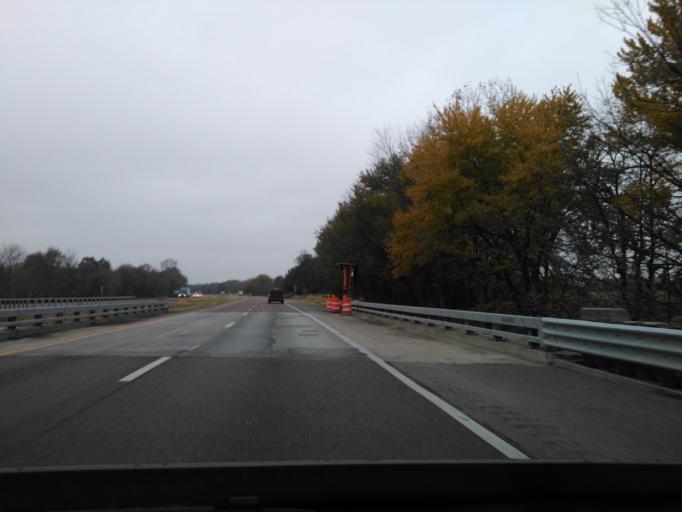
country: US
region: Illinois
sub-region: Madison County
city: Troy
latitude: 38.7623
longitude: -89.8238
